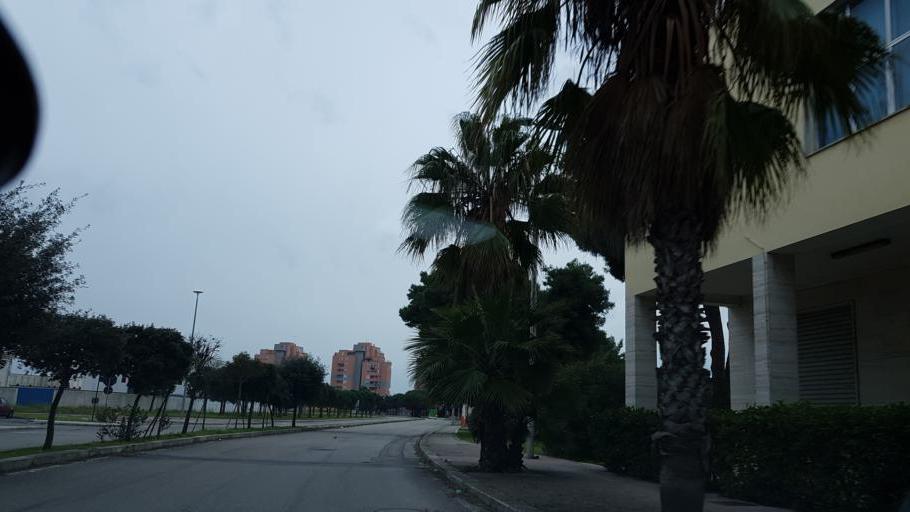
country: IT
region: Apulia
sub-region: Provincia di Brindisi
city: Brindisi
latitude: 40.6358
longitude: 17.9543
